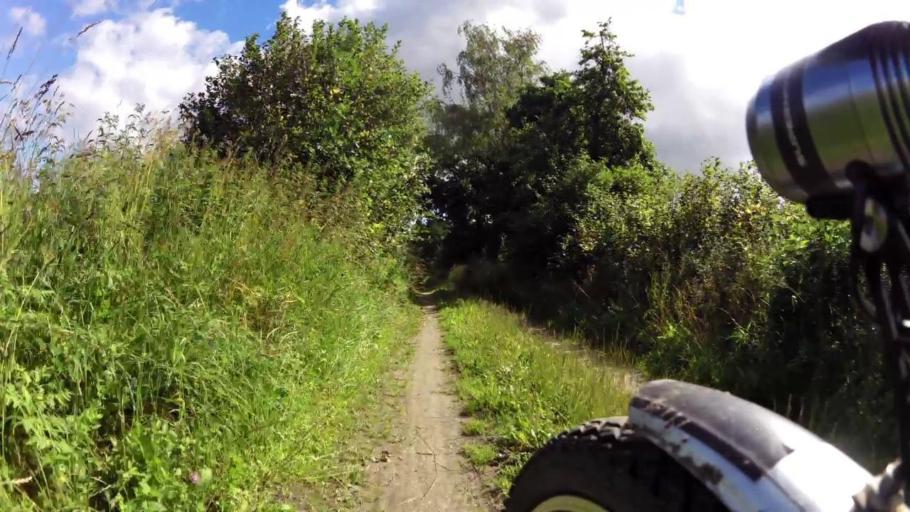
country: PL
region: West Pomeranian Voivodeship
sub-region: Powiat swidwinski
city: Rabino
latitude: 53.8238
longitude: 15.9088
